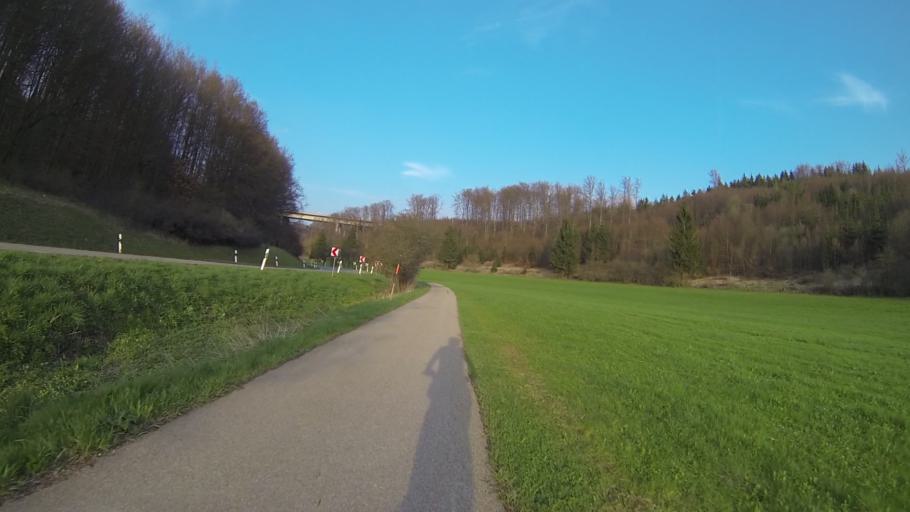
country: DE
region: Baden-Wuerttemberg
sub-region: Regierungsbezirk Stuttgart
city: Nattheim
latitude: 48.6982
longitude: 10.2104
